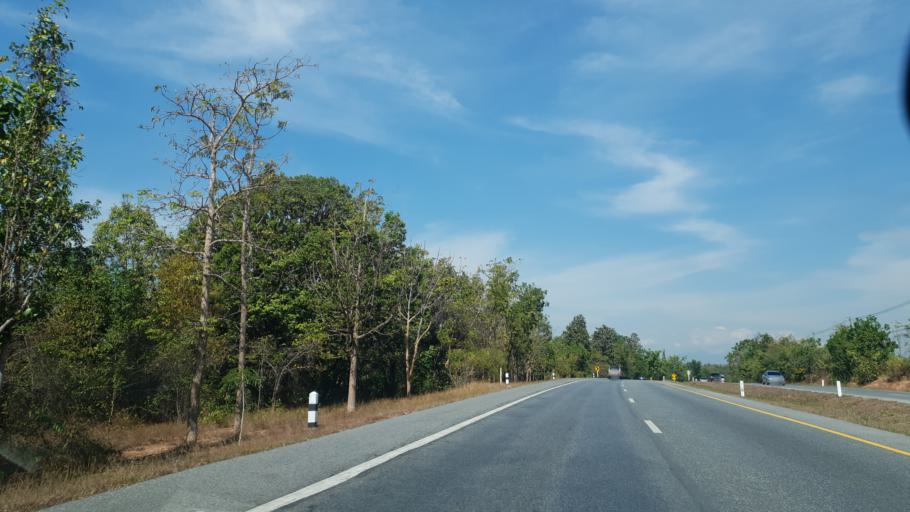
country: TH
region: Uttaradit
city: Thong Saen Khan
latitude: 17.4229
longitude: 100.2258
